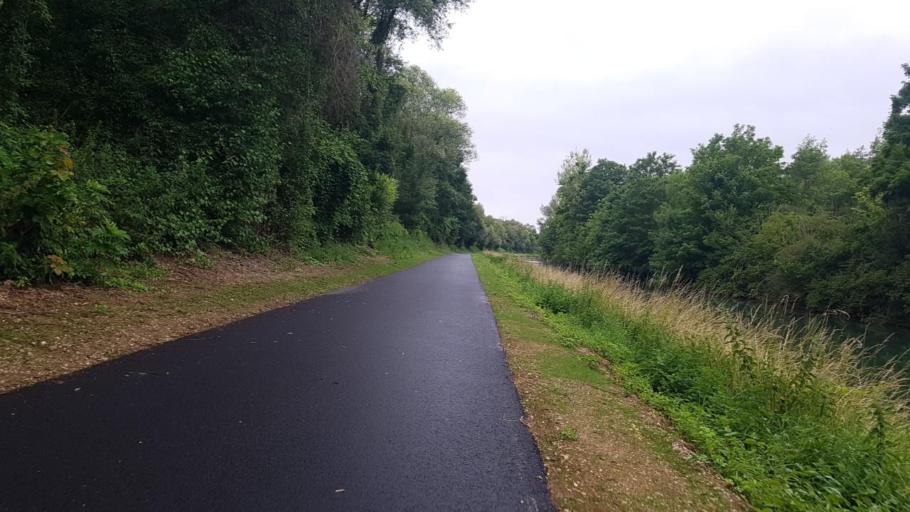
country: FR
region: Champagne-Ardenne
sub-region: Departement de la Marne
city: Vitry-le-Francois
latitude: 48.7747
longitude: 4.5456
